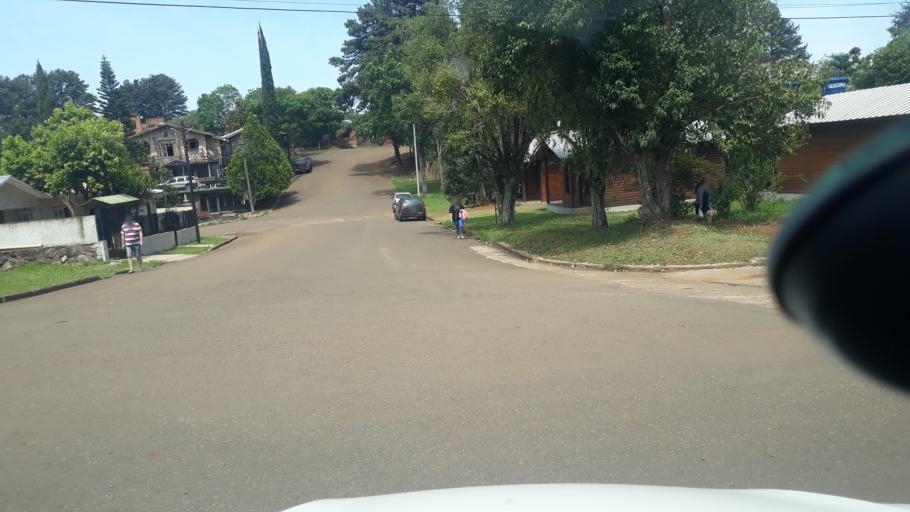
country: AR
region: Misiones
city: Bernardo de Irigoyen
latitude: -26.2526
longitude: -53.6488
